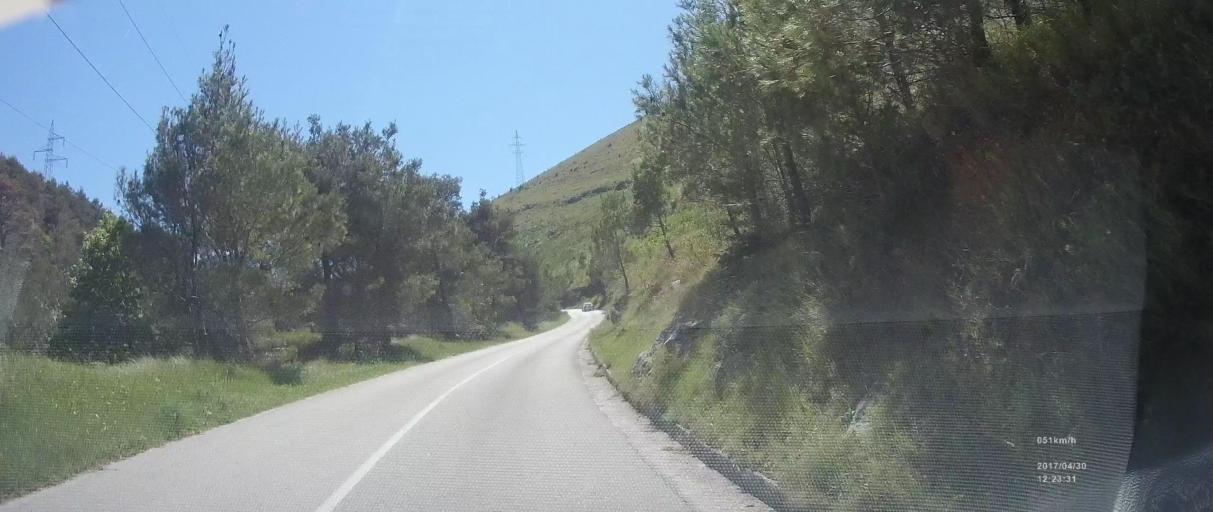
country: HR
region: Splitsko-Dalmatinska
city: Zrnovnica
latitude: 43.5161
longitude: 16.5788
